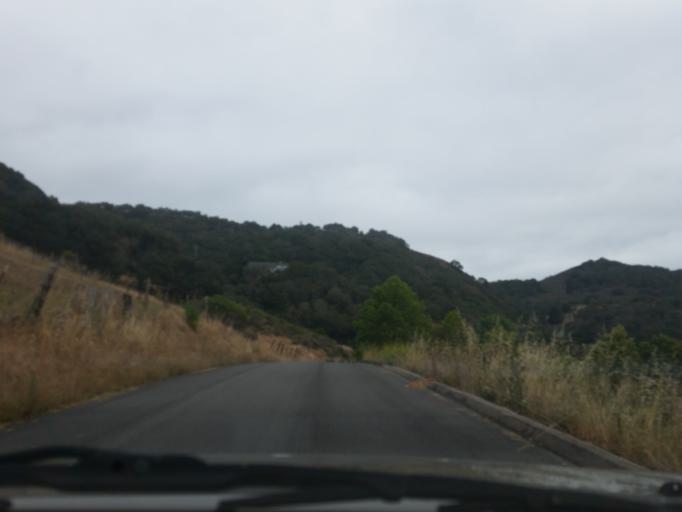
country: US
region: California
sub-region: San Luis Obispo County
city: Avila Beach
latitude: 35.1873
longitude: -120.6967
